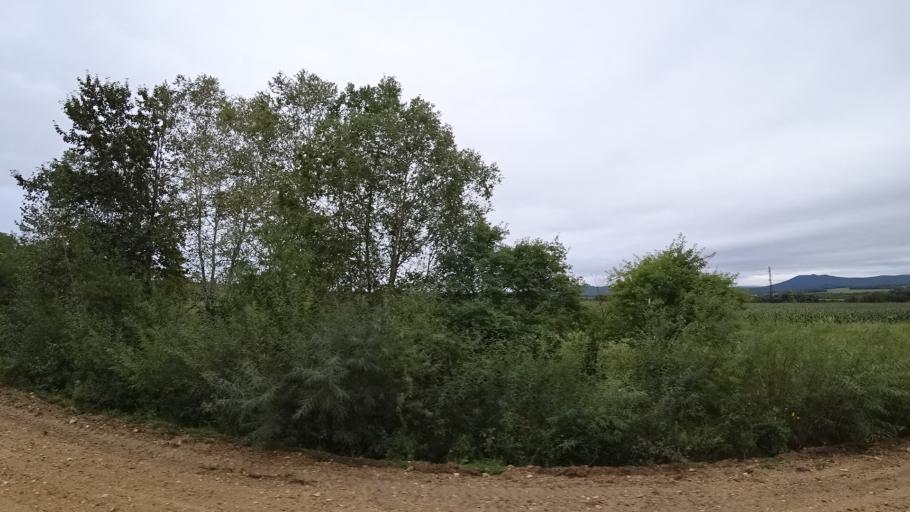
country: RU
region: Primorskiy
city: Rettikhovka
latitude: 44.1519
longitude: 132.6791
